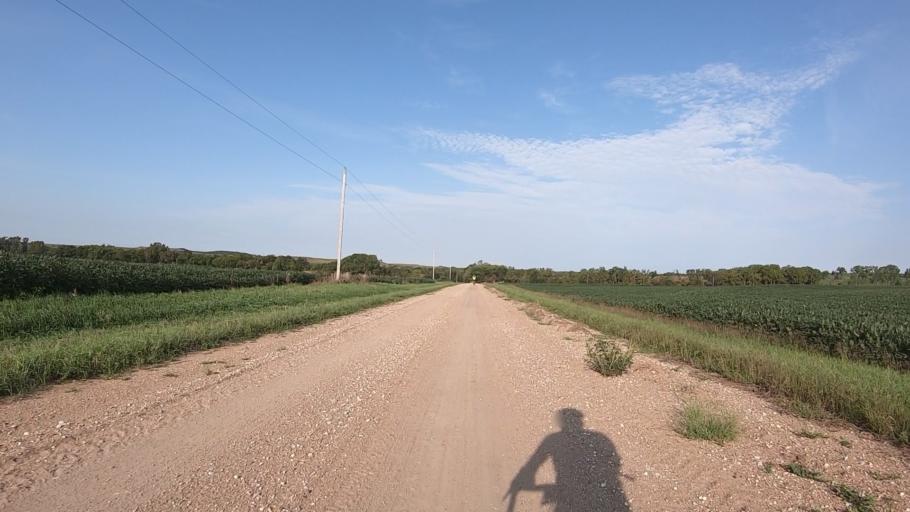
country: US
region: Kansas
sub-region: Marshall County
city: Blue Rapids
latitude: 39.6533
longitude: -96.8591
